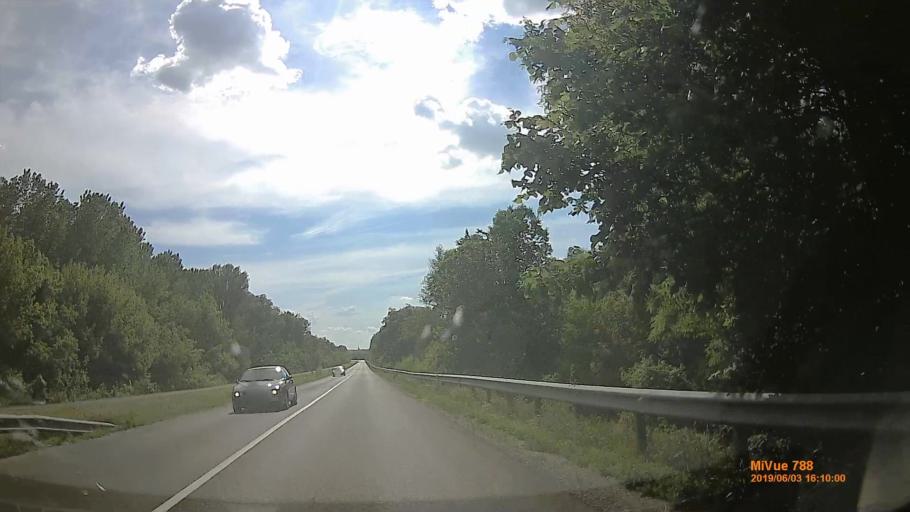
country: HU
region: Tolna
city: Dunafoldvar
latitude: 46.8165
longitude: 18.9519
